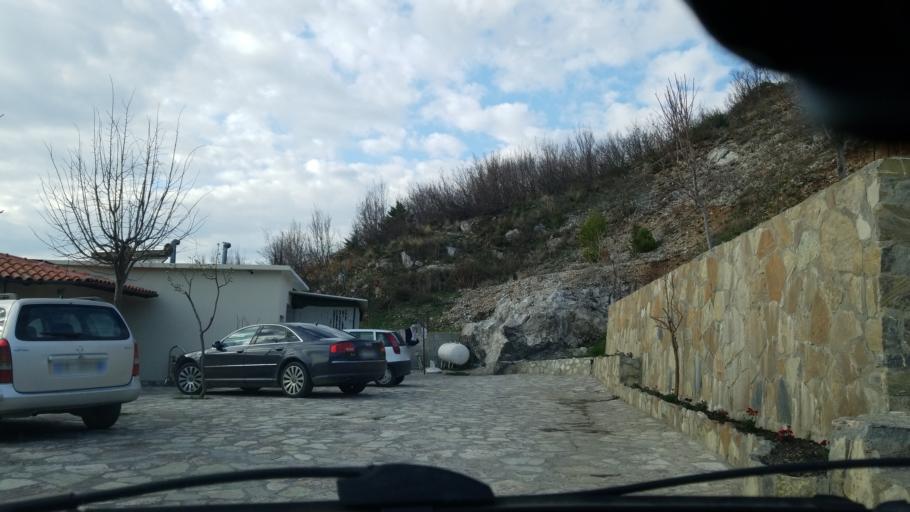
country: AL
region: Lezhe
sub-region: Rrethi i Lezhes
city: Kallmeti i Madh
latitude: 41.8743
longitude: 19.6964
